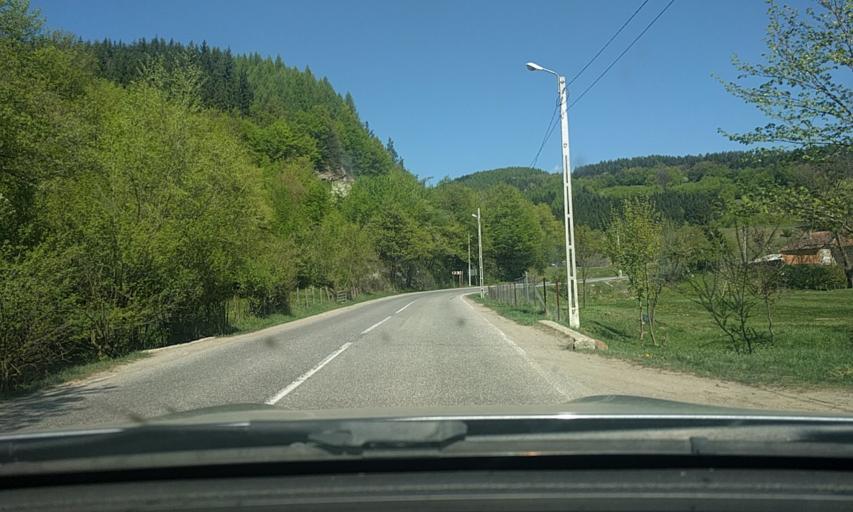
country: RO
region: Covasna
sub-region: Comuna Dobarlau
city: Dobarlau
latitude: 45.6815
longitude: 25.9276
